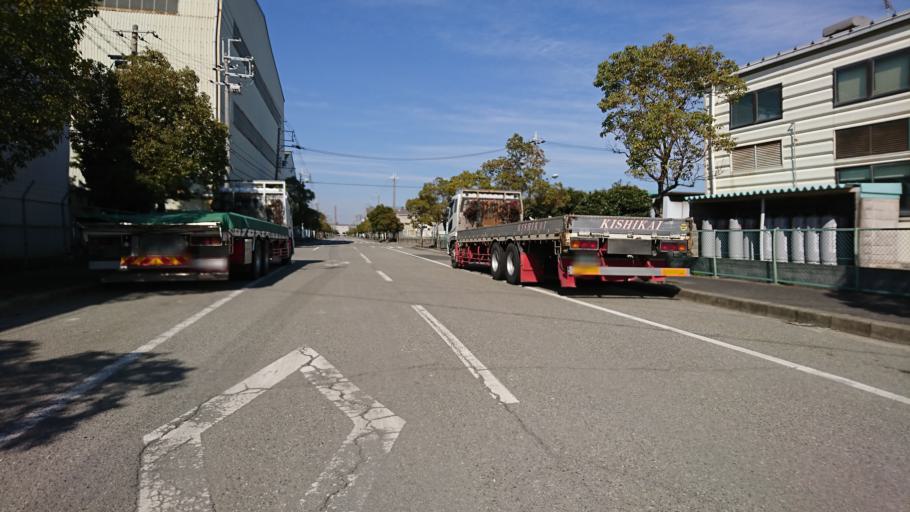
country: JP
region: Hyogo
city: Kakogawacho-honmachi
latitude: 34.6961
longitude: 134.8470
